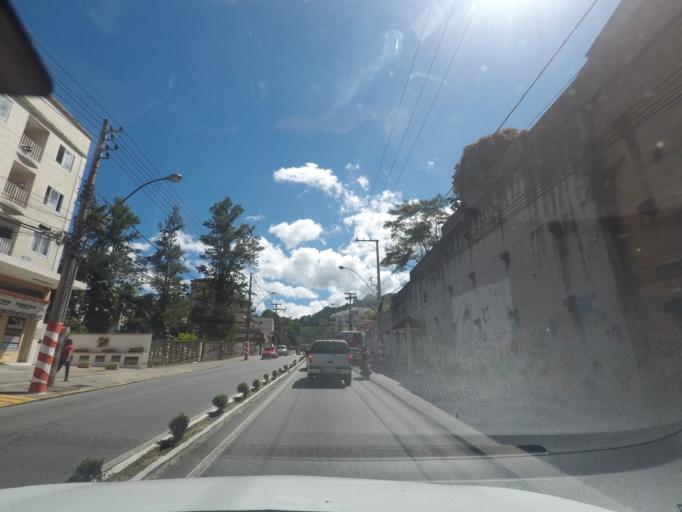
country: BR
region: Rio de Janeiro
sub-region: Teresopolis
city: Teresopolis
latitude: -22.4252
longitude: -42.9791
